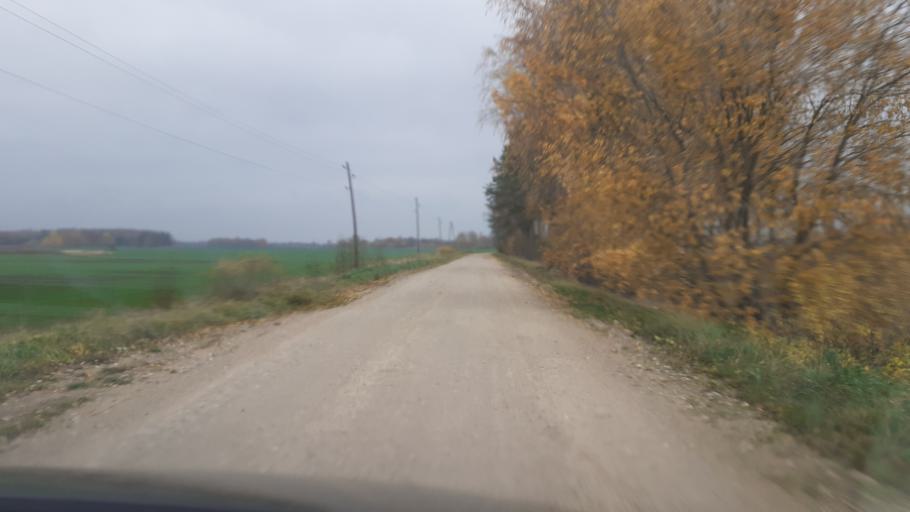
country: LV
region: Saldus Rajons
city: Saldus
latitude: 56.8666
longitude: 22.3068
